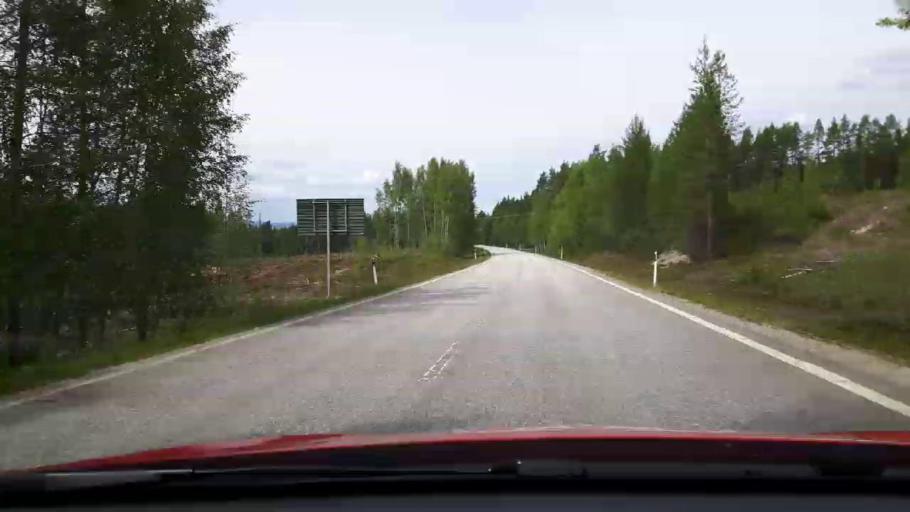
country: SE
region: Jaemtland
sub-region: Harjedalens Kommun
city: Sveg
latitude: 62.1225
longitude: 14.1619
